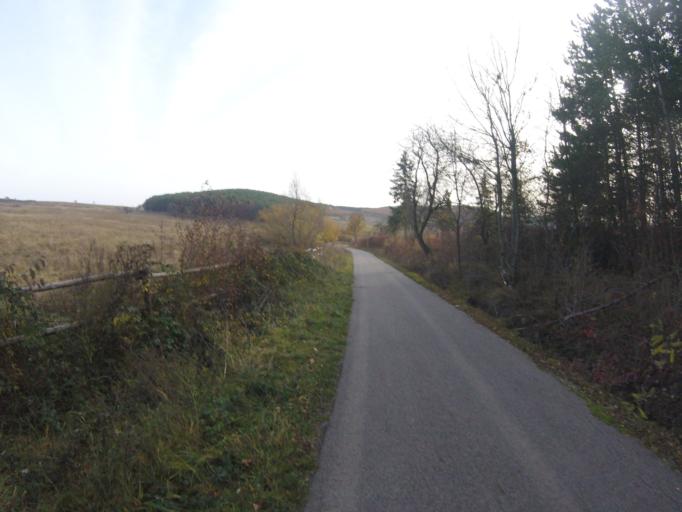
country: HU
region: Borsod-Abauj-Zemplen
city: Gonc
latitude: 48.5171
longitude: 21.4577
